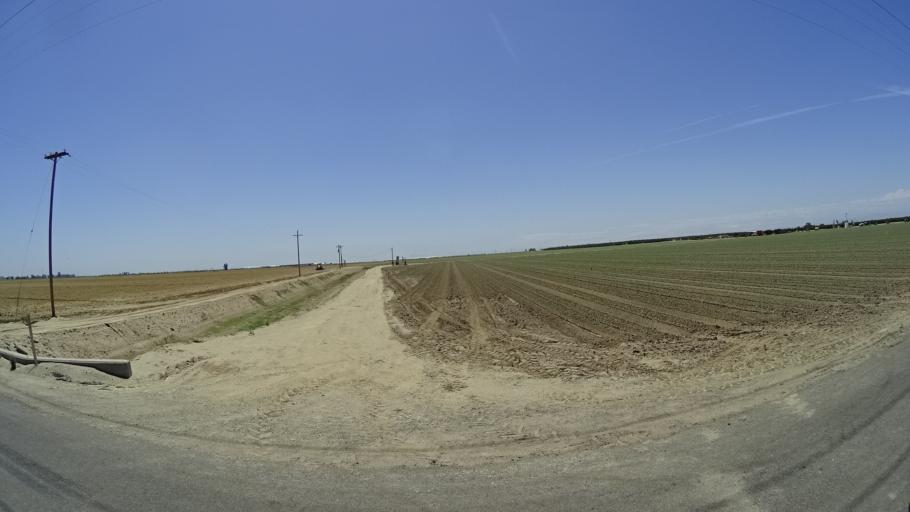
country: US
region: California
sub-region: Kings County
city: Armona
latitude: 36.2402
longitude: -119.6960
